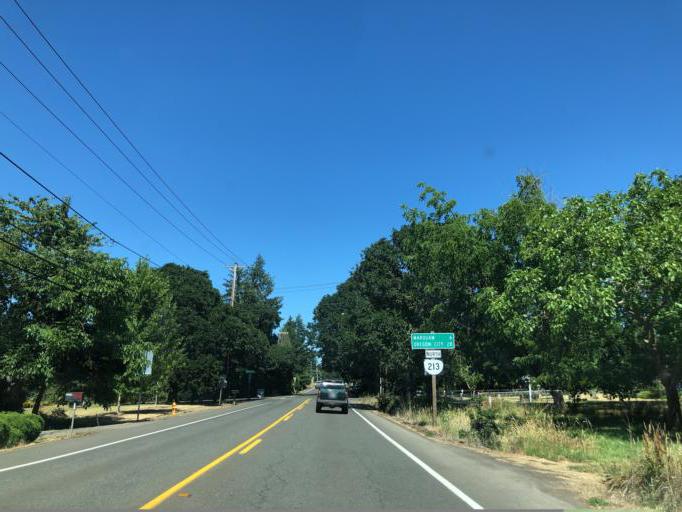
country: US
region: Oregon
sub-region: Marion County
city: Silverton
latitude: 45.0125
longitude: -122.7697
